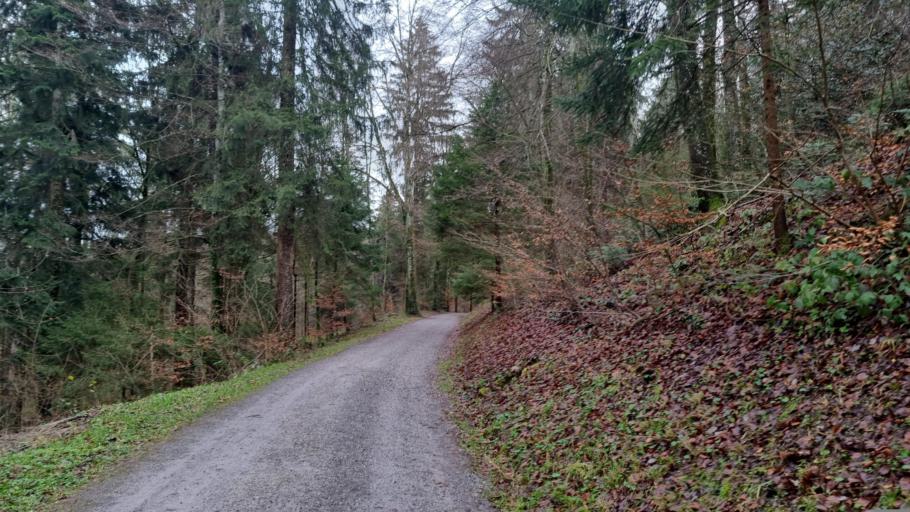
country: CH
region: Zurich
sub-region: Bezirk Zuerich
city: Zuerich (Kreis 9) / Albisrieden
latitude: 47.3639
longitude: 8.4801
